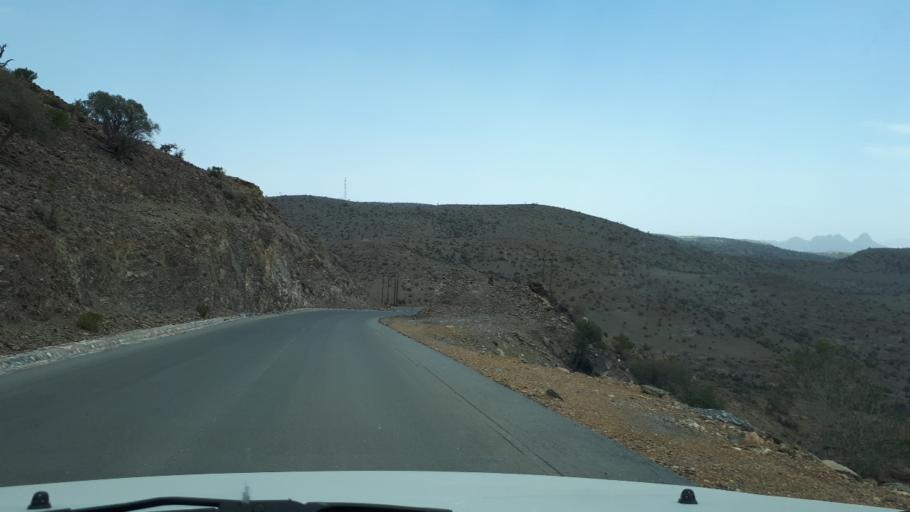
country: OM
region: Al Batinah
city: Rustaq
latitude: 23.2311
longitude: 57.1989
